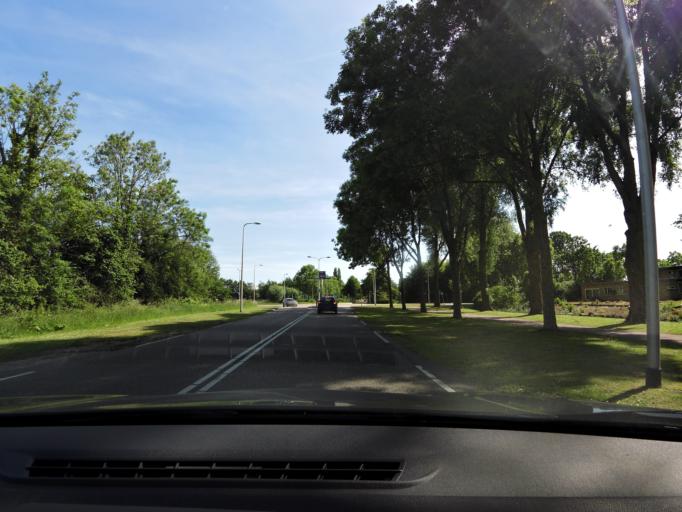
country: NL
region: South Holland
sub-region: Gemeente Albrandswaard
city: Rhoon
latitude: 51.8600
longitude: 4.4335
